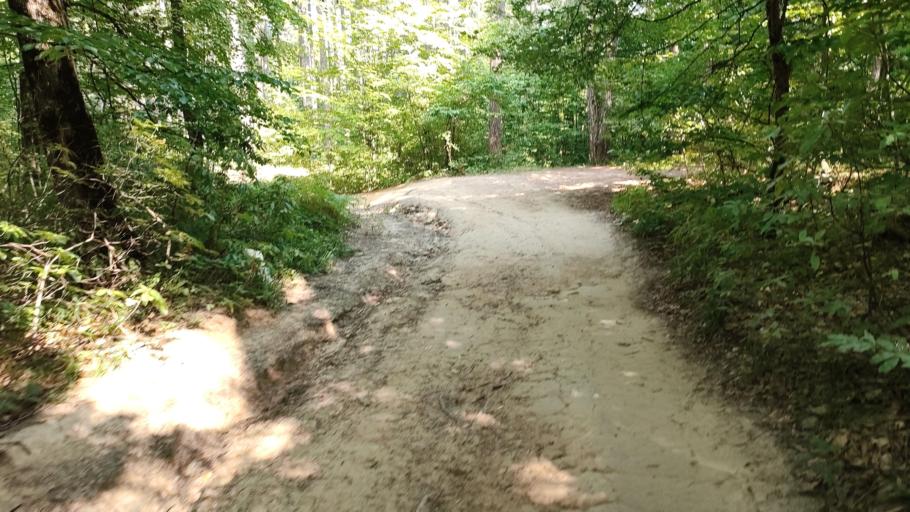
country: RU
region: Krasnodarskiy
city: Goryachiy Klyuch
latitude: 44.6110
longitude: 39.1035
